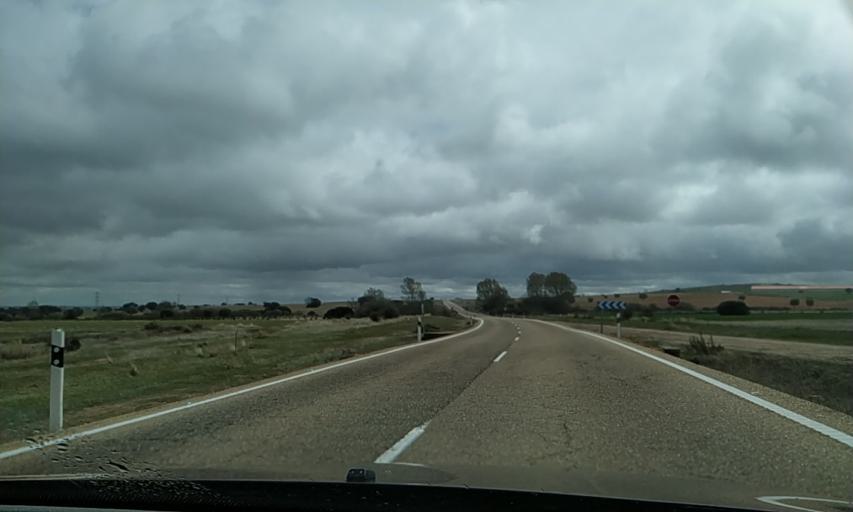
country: ES
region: Castille and Leon
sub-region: Provincia de Zamora
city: Tabara
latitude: 41.8543
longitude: -5.9917
